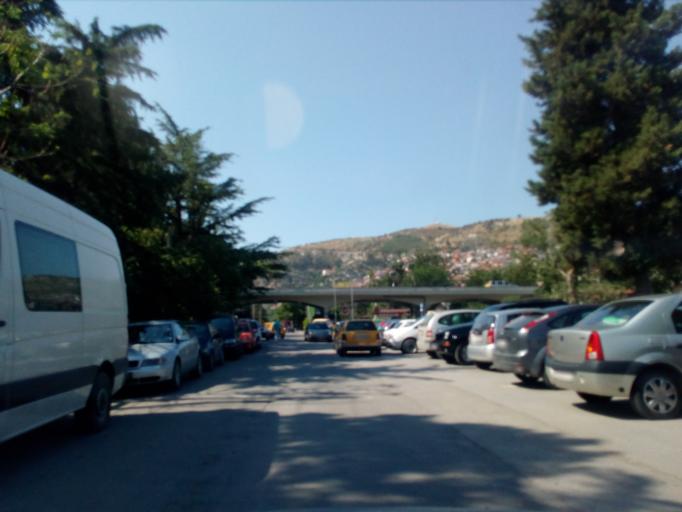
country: MK
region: Veles
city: Veles
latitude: 41.7162
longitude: 21.7868
